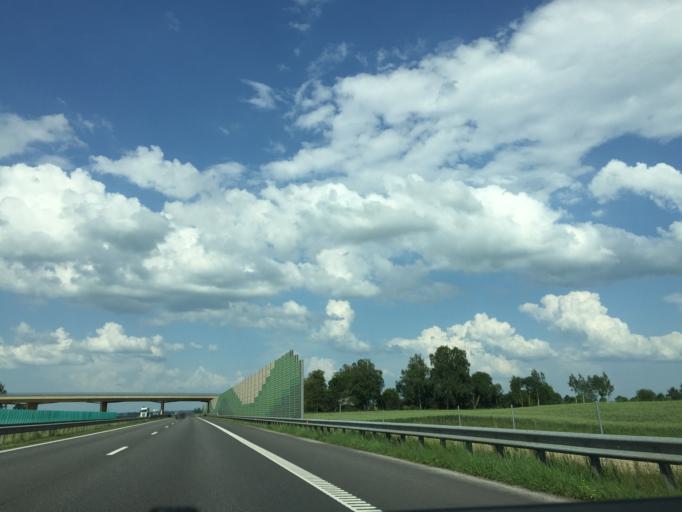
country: LT
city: Kazlu Ruda
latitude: 54.6799
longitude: 23.5810
